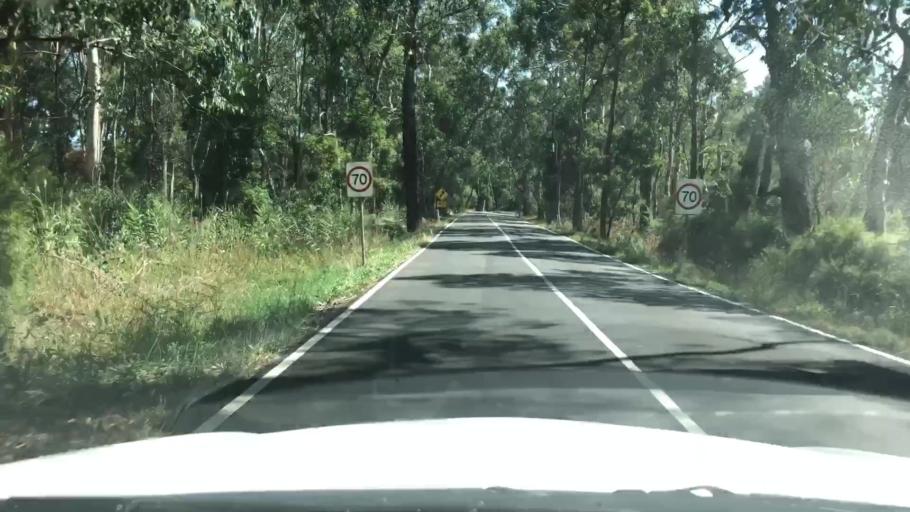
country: AU
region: Victoria
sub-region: Yarra Ranges
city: Woori Yallock
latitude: -37.8142
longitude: 145.5023
